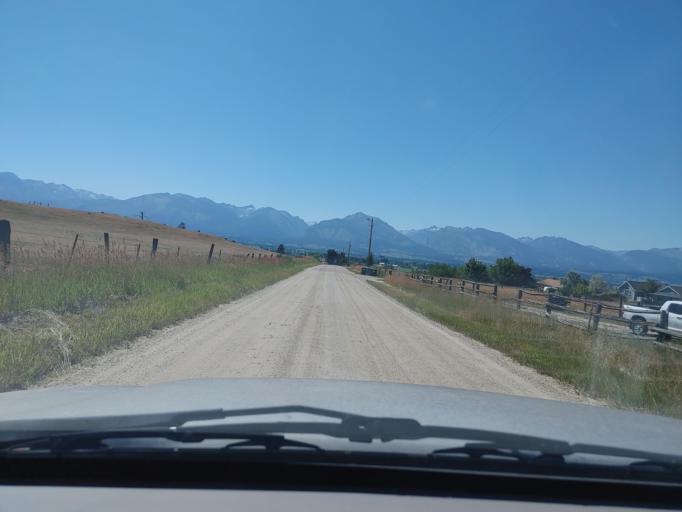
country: US
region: Montana
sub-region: Ravalli County
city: Hamilton
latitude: 46.2765
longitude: -114.0205
